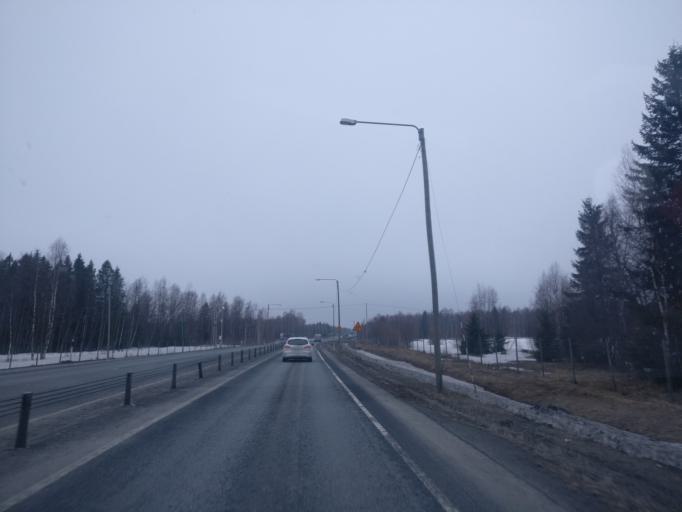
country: FI
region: Lapland
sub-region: Kemi-Tornio
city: Simo
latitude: 65.6690
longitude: 24.9324
